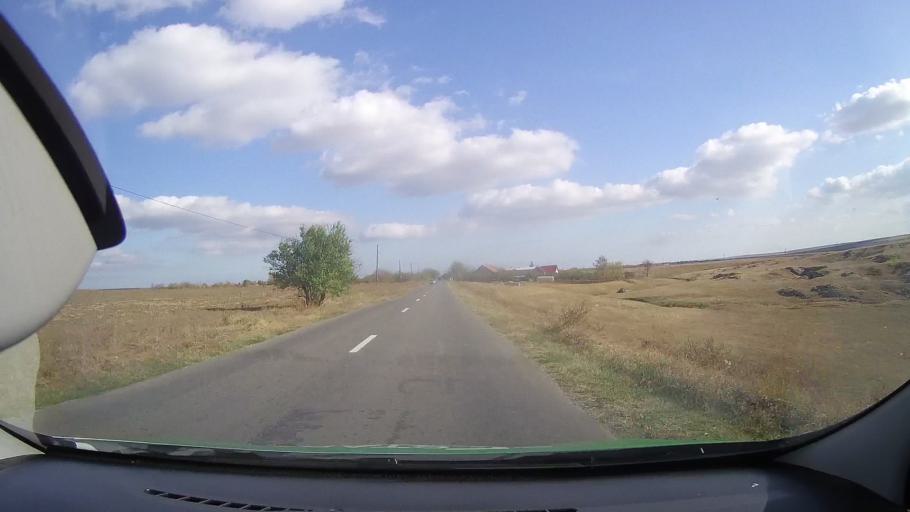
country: RO
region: Constanta
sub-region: Comuna Cogealac
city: Cogealac
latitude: 44.5613
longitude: 28.5814
